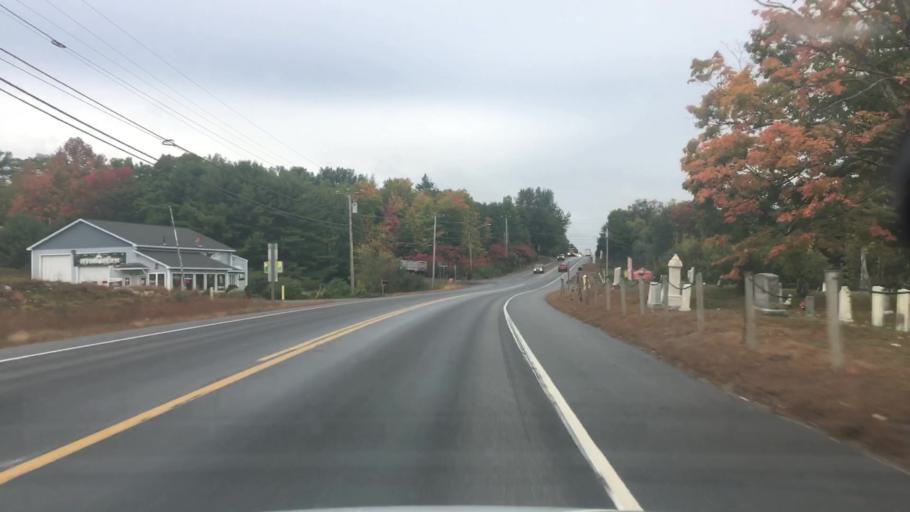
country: US
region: Maine
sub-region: Kennebec County
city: Belgrade
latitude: 44.3870
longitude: -69.8025
